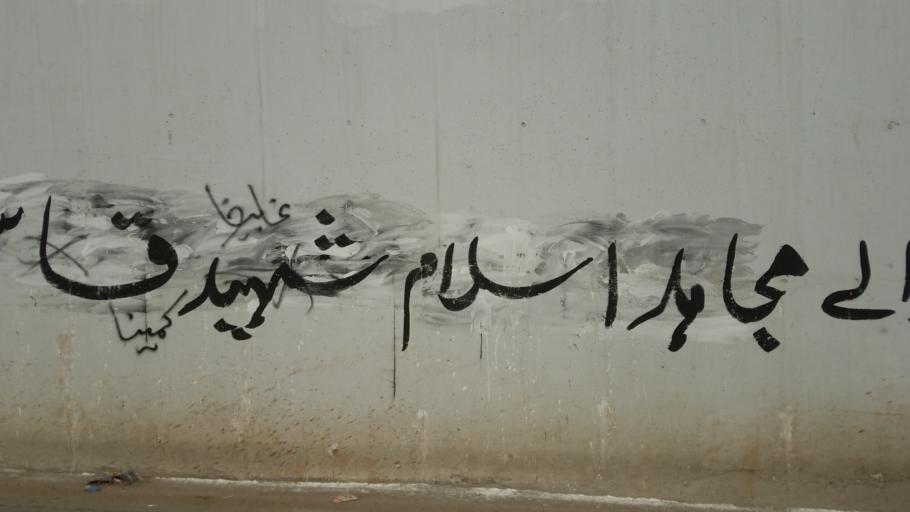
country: PK
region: Sindh
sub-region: Karachi District
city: Karachi
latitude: 24.8782
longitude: 67.0386
